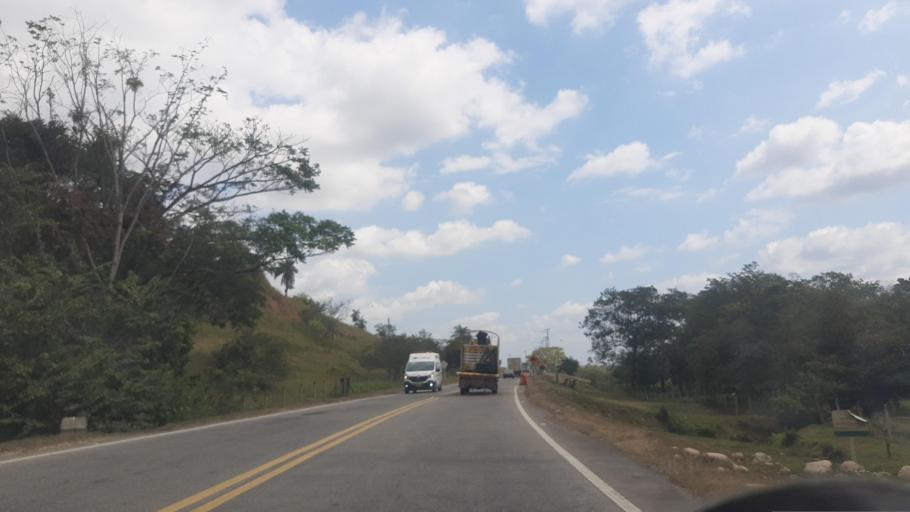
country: CO
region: Casanare
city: Tauramena
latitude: 5.0153
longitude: -72.6756
